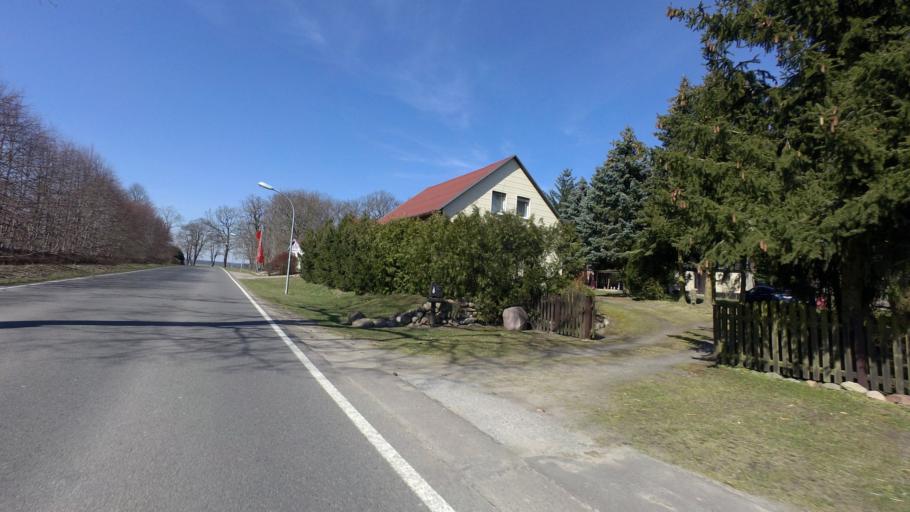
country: DE
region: Brandenburg
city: Protzel
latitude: 52.6312
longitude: 14.0123
